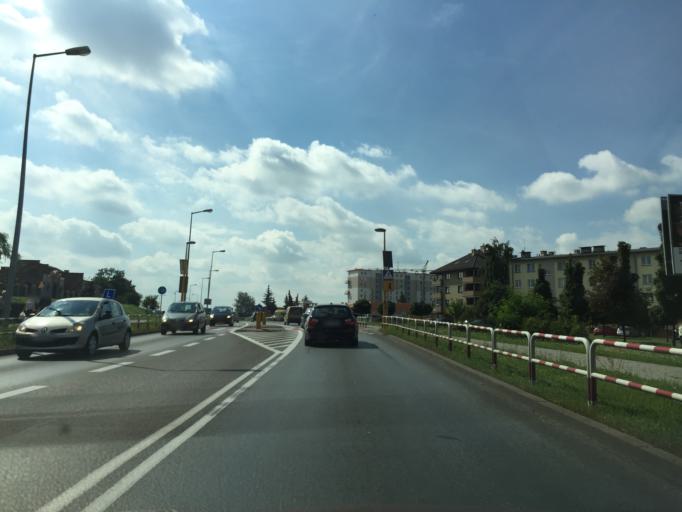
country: PL
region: Greater Poland Voivodeship
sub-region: Kalisz
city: Kalisz
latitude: 51.7518
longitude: 18.0612
